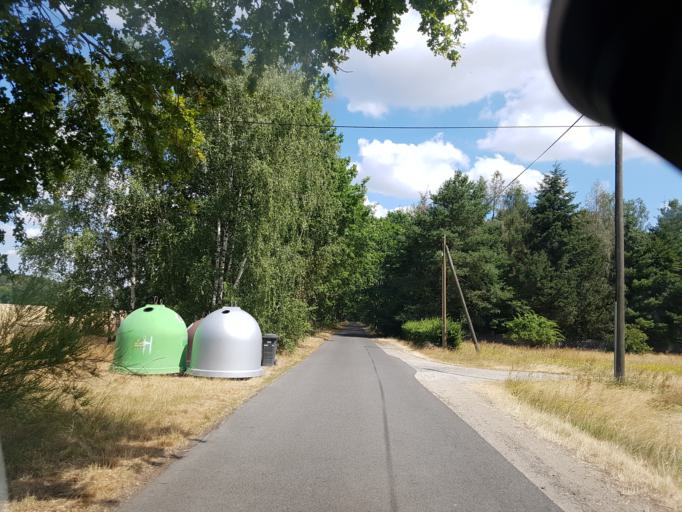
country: DE
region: Brandenburg
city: Cottbus
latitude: 51.6892
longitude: 14.3111
